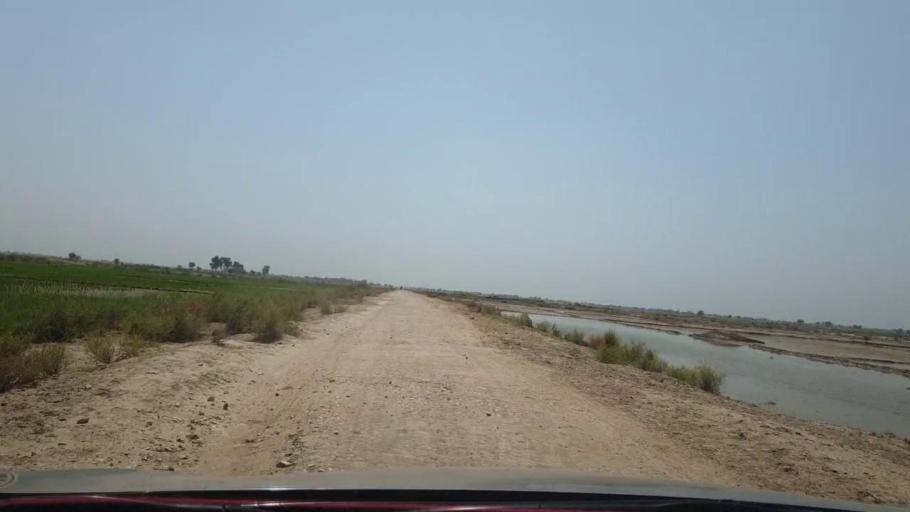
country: PK
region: Sindh
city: Kambar
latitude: 27.5853
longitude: 67.8763
